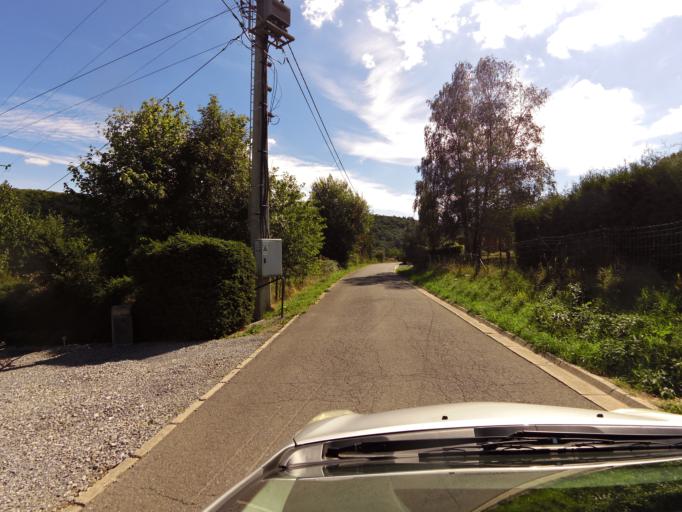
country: BE
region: Wallonia
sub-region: Province du Luxembourg
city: Rendeux
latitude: 50.2270
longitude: 5.5216
